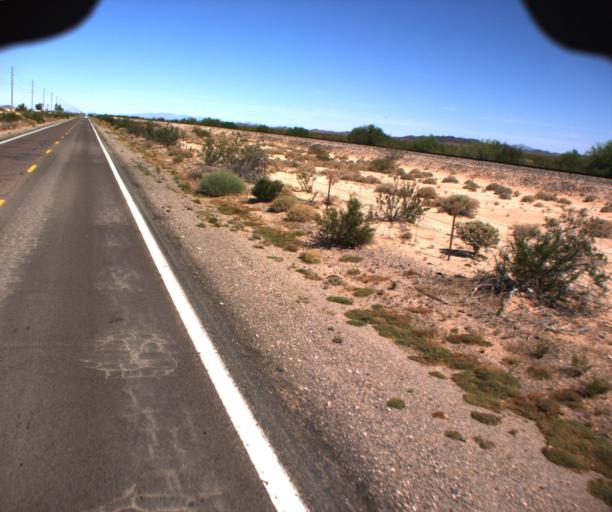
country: US
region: Arizona
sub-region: La Paz County
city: Salome
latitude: 33.8597
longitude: -113.9164
